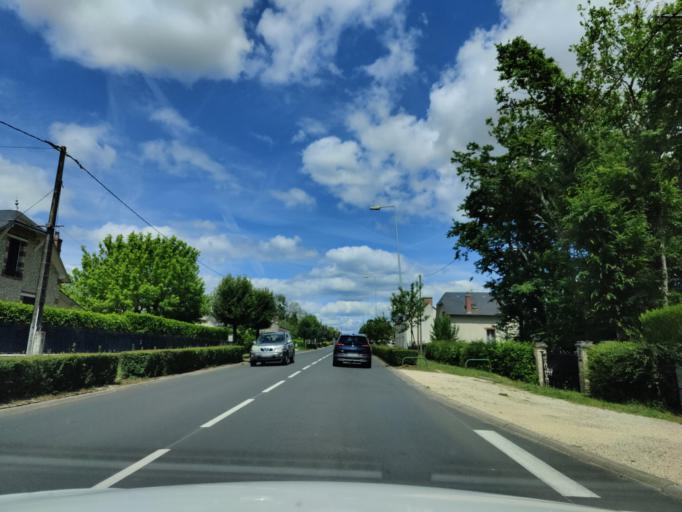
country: FR
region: Centre
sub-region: Departement du Cher
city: Vasselay
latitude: 47.1968
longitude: 2.4237
